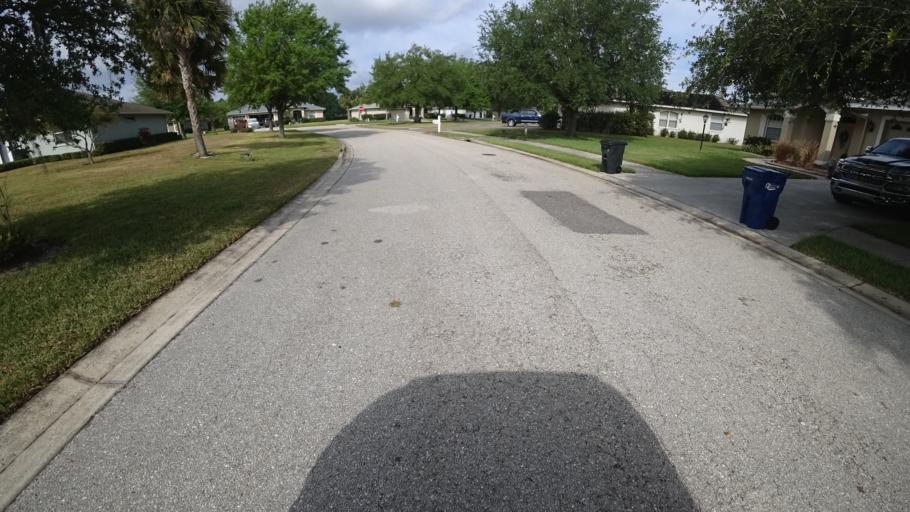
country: US
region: Florida
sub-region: Manatee County
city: Ellenton
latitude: 27.5718
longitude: -82.4711
